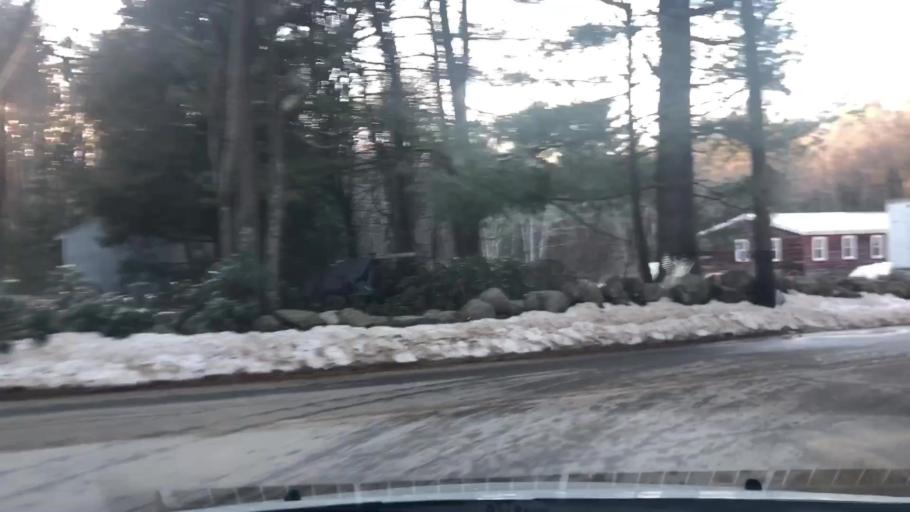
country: US
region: New Hampshire
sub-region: Hillsborough County
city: Milford
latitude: 42.8017
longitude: -71.6454
